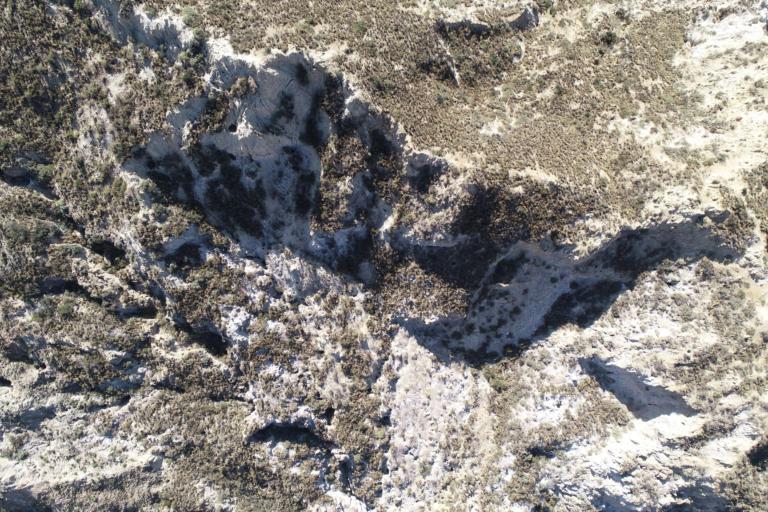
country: BO
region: La Paz
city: La Paz
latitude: -16.5509
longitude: -68.1095
